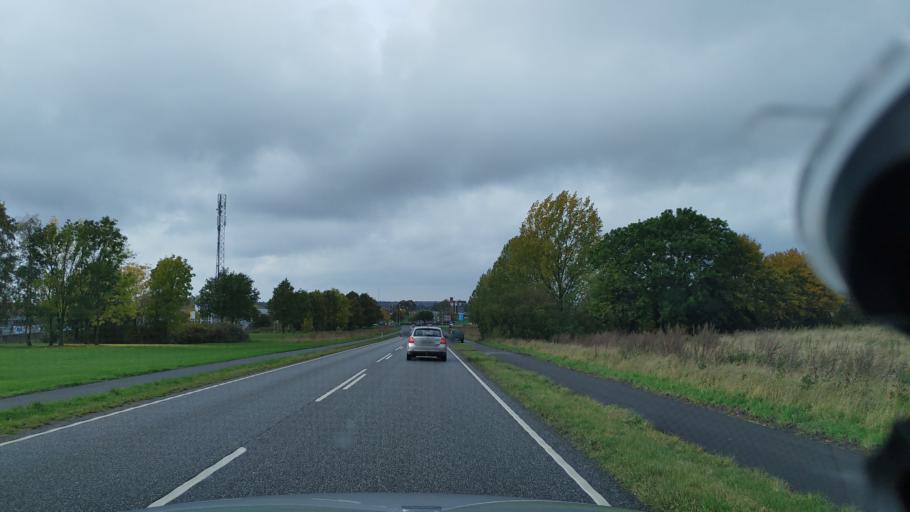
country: DK
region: Zealand
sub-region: Naestved Kommune
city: Fensmark
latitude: 55.2534
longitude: 11.7935
